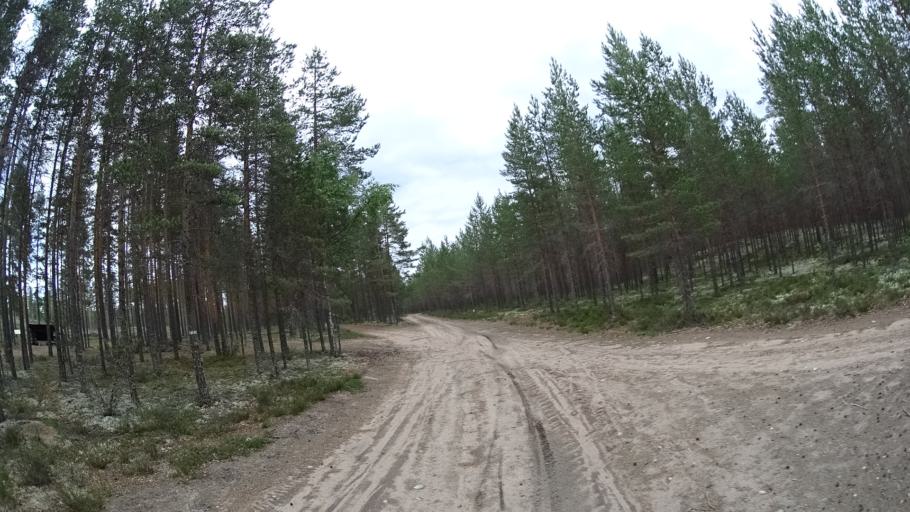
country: FI
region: Satakunta
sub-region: Pohjois-Satakunta
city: Jaemijaervi
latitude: 61.7594
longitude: 22.7814
